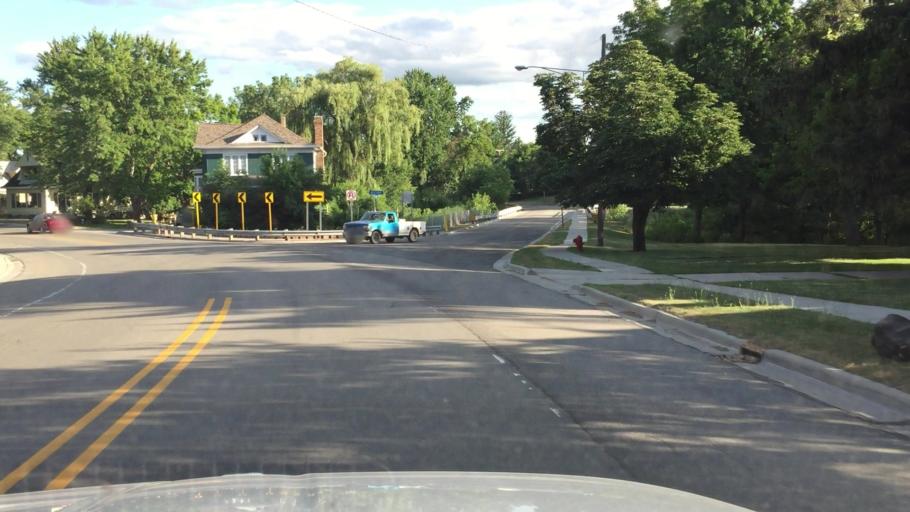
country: US
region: Michigan
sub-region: Saint Clair County
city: Yale
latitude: 43.1260
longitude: -82.7981
